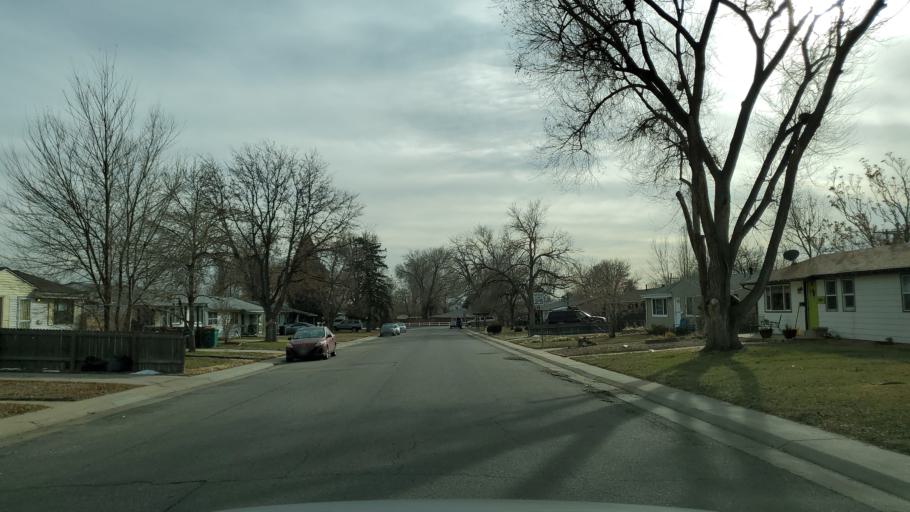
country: US
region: Colorado
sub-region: Adams County
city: Twin Lakes
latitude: 39.8288
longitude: -105.0193
